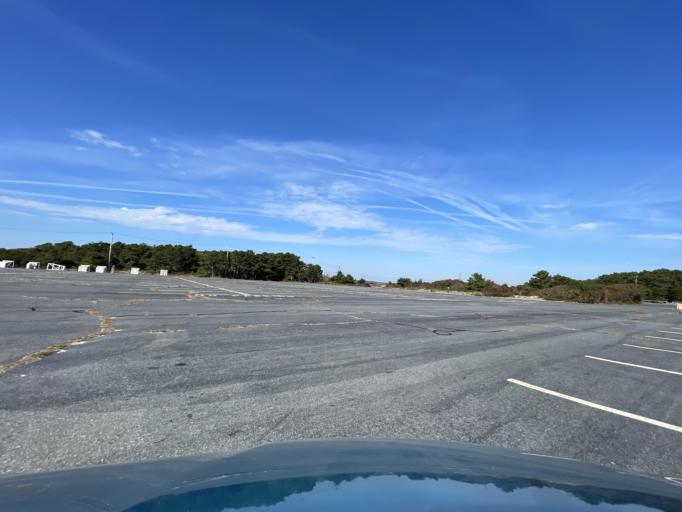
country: US
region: Massachusetts
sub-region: Bristol County
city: Head of Westport
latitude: 41.5063
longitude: -71.0503
